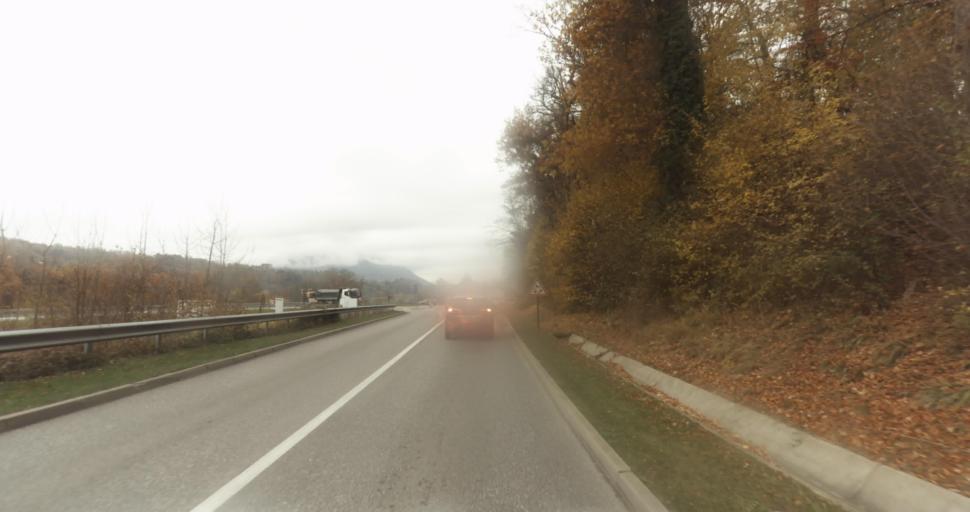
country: FR
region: Rhone-Alpes
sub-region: Departement de la Haute-Savoie
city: Saint-Martin-Bellevue
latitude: 45.9604
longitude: 6.1656
